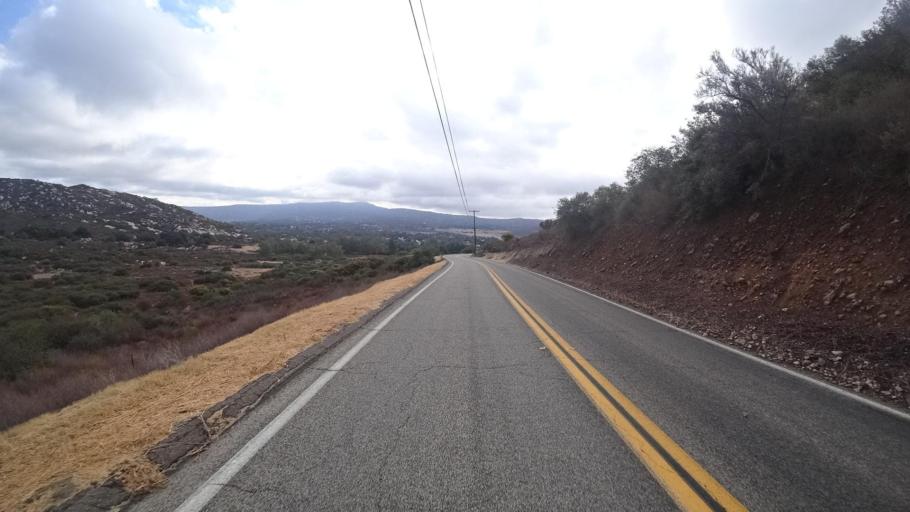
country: MX
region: Baja California
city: Tecate
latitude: 32.6259
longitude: -116.6263
